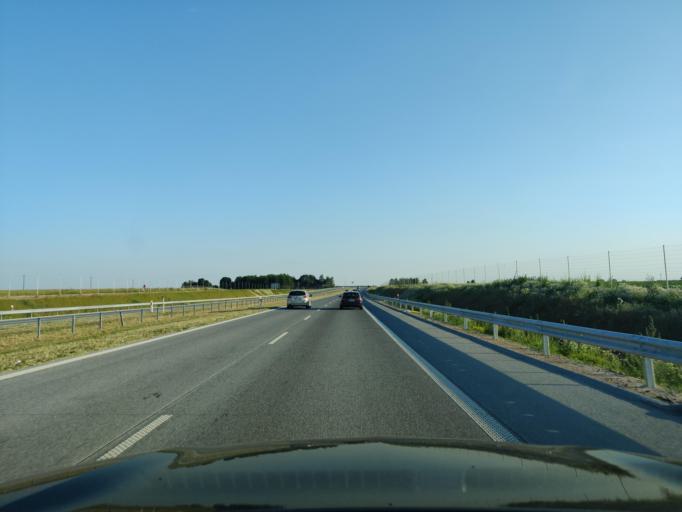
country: PL
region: Masovian Voivodeship
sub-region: Powiat mlawski
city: Wisniewo
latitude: 53.0400
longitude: 20.3558
